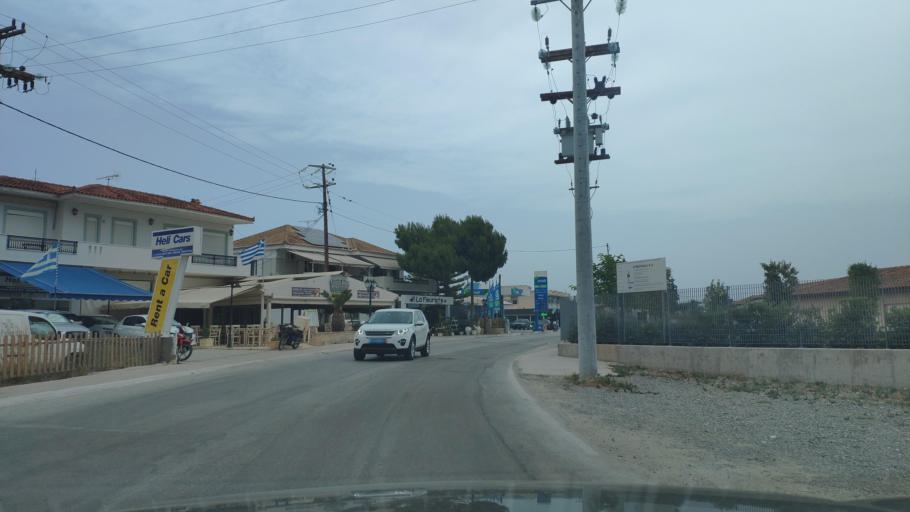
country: GR
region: Peloponnese
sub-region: Nomos Argolidos
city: Porto Cheli
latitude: 37.3280
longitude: 23.1446
